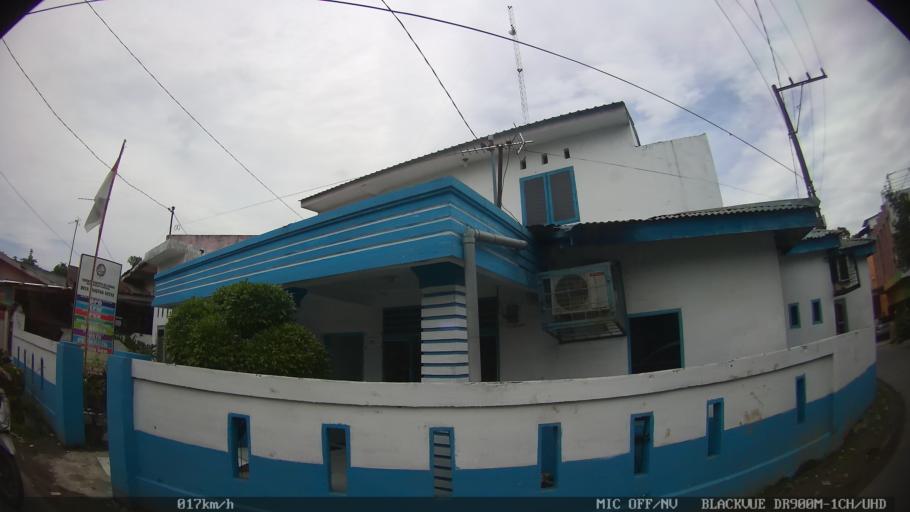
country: ID
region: North Sumatra
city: Sunggal
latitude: 3.6170
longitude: 98.5999
